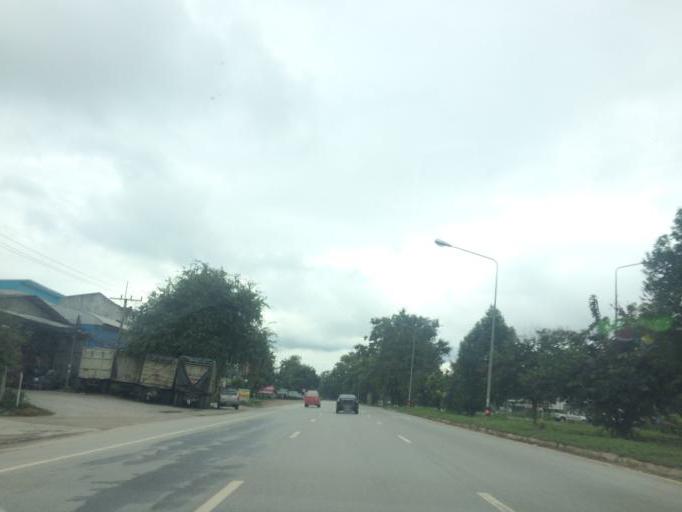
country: TH
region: Chiang Rai
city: Chiang Rai
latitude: 19.8612
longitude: 99.8200
